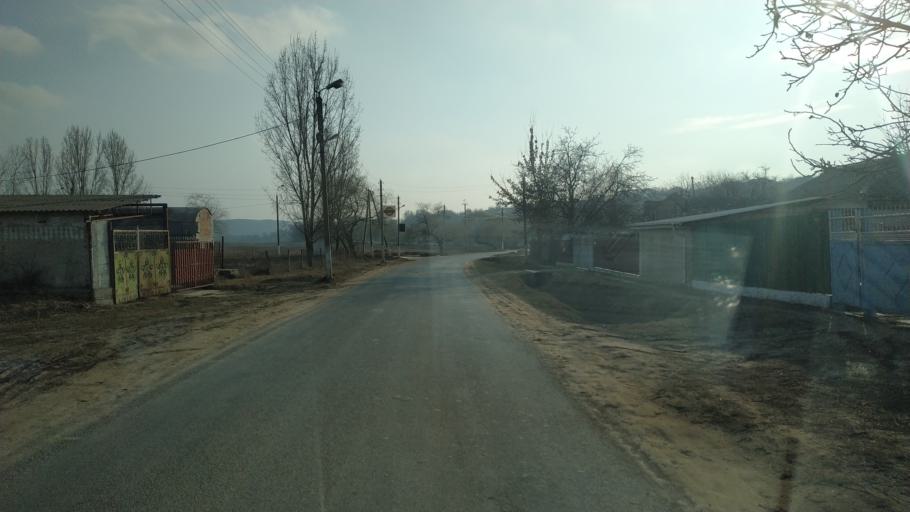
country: MD
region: Hincesti
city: Dancu
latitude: 46.7772
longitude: 28.3475
